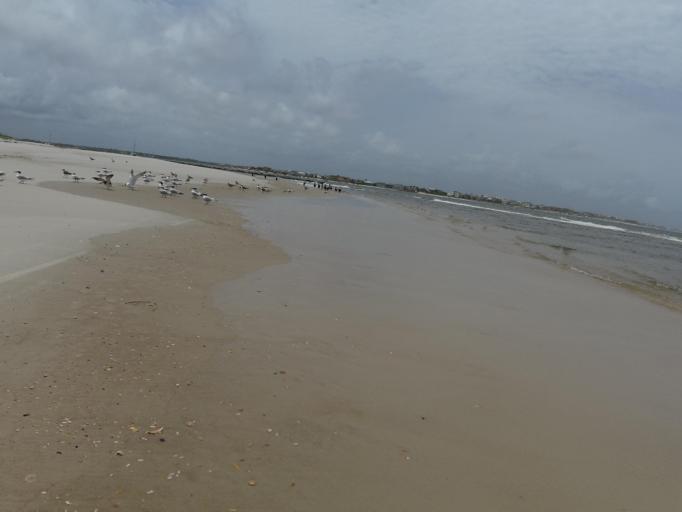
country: US
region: Florida
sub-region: Saint Johns County
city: Saint Augustine
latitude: 29.9080
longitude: -81.2827
